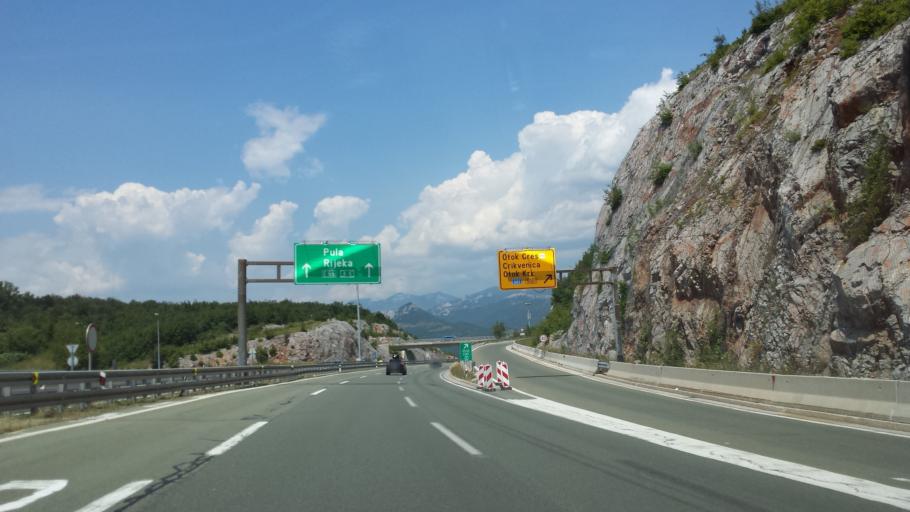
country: HR
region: Primorsko-Goranska
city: Krasica
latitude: 45.3324
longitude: 14.5983
